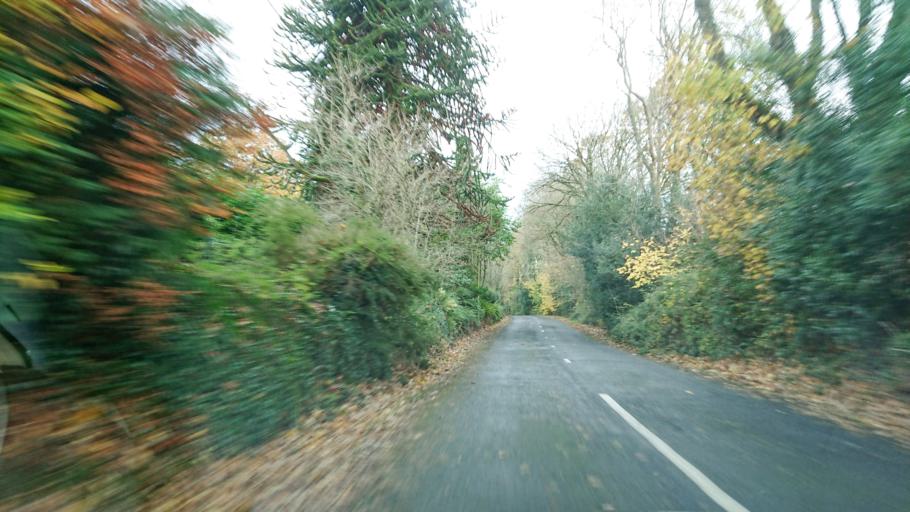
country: IE
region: Munster
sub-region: South Tipperary
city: Cluain Meala
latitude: 52.3545
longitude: -7.6363
